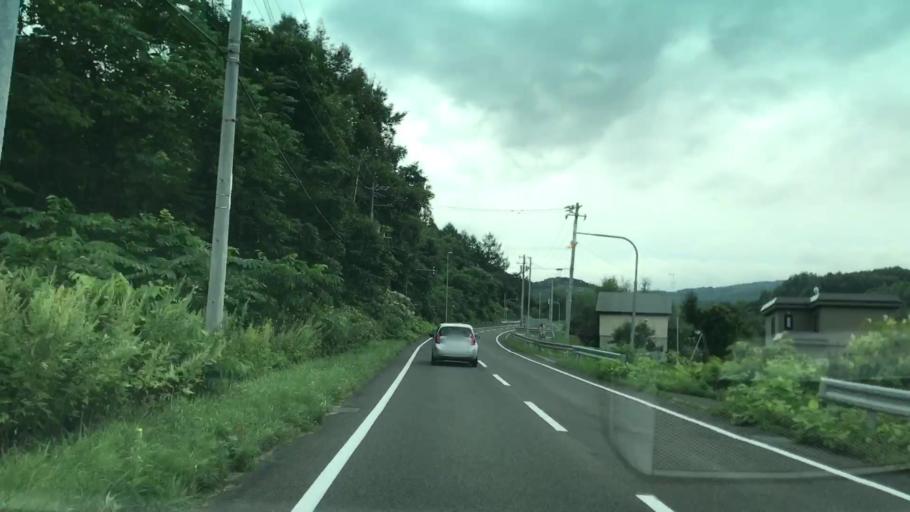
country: JP
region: Hokkaido
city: Yoichi
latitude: 43.1516
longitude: 140.8220
